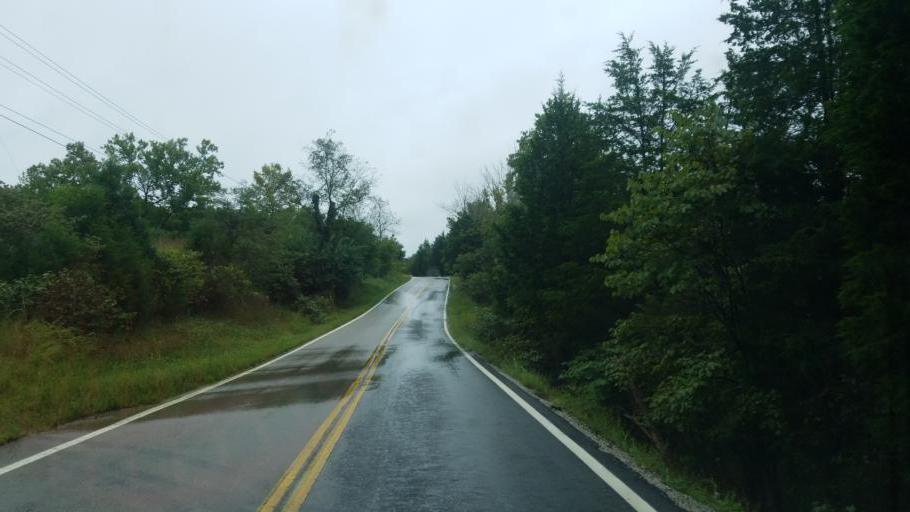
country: US
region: Ohio
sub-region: Adams County
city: West Union
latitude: 38.7732
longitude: -83.5326
